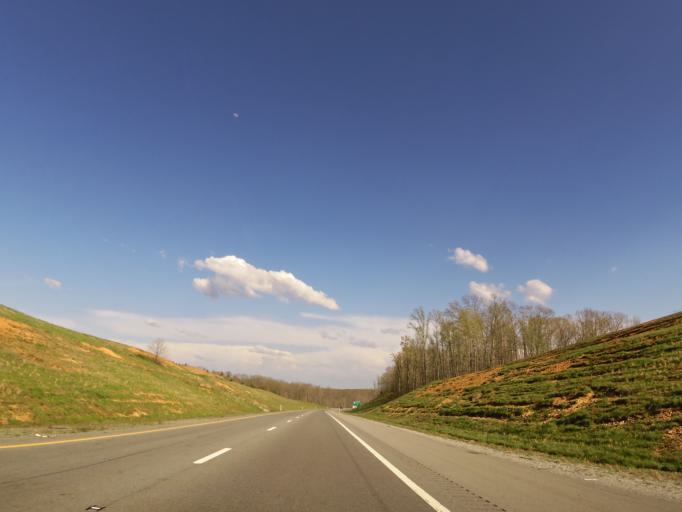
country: US
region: Tennessee
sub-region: Williamson County
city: Fairview
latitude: 35.8889
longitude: -87.1175
